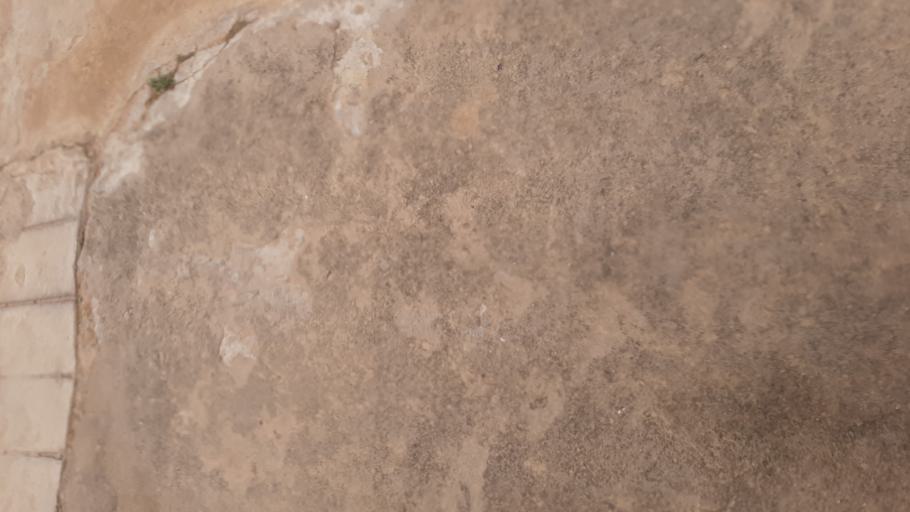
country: IN
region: Telangana
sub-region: Medak
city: Medak
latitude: 18.0439
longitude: 78.2664
